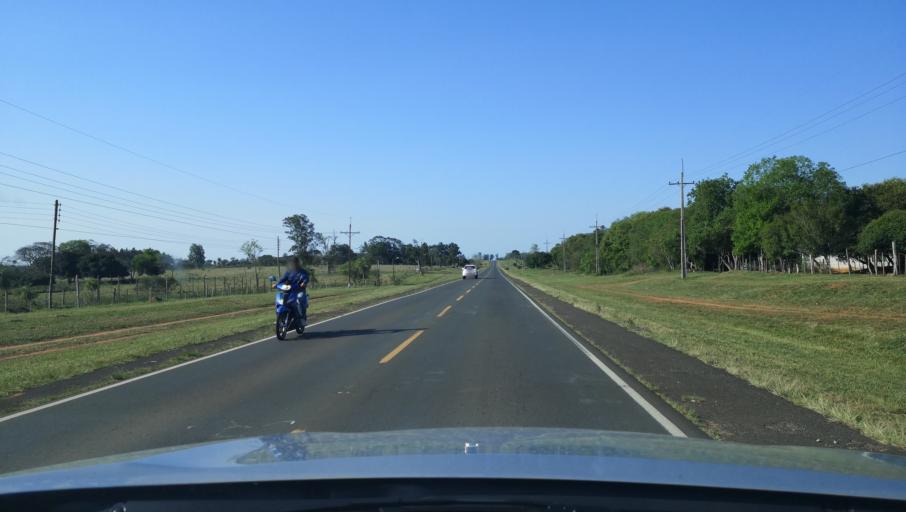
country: PY
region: Misiones
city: Santa Maria
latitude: -26.8198
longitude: -57.0260
